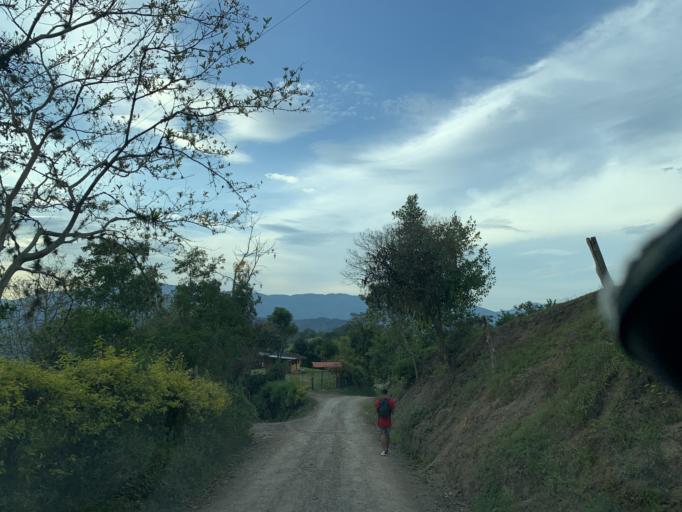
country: CO
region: Boyaca
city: Santana
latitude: 6.0839
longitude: -73.4955
